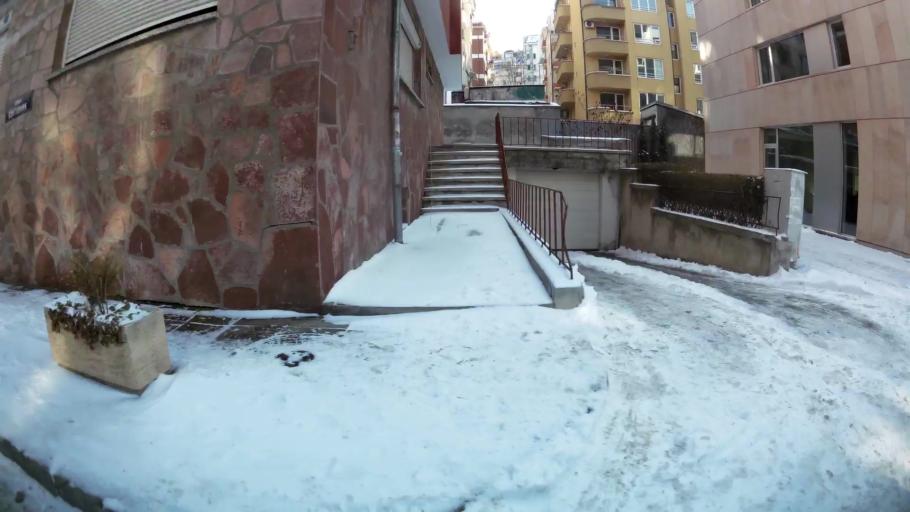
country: BG
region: Sofia-Capital
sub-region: Stolichna Obshtina
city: Sofia
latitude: 42.6716
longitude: 23.3143
